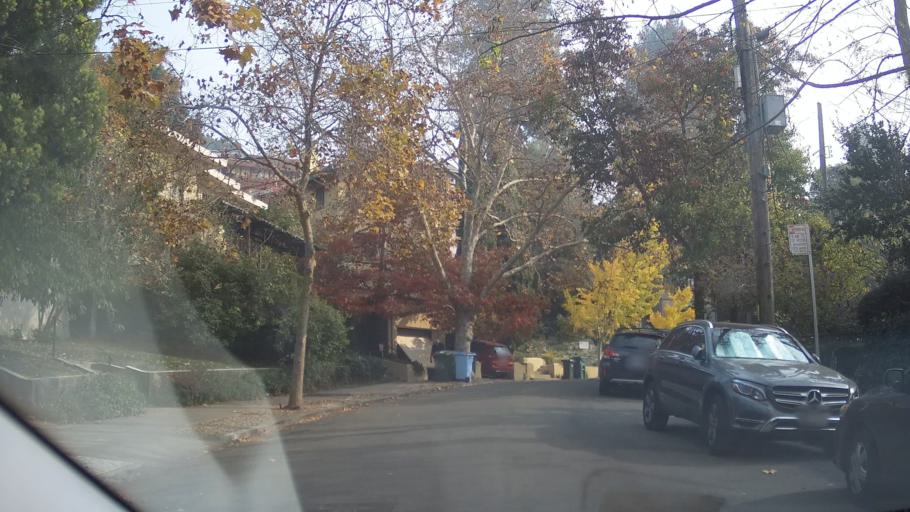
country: US
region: California
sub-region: Alameda County
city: Piedmont
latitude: 37.8551
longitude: -122.2428
